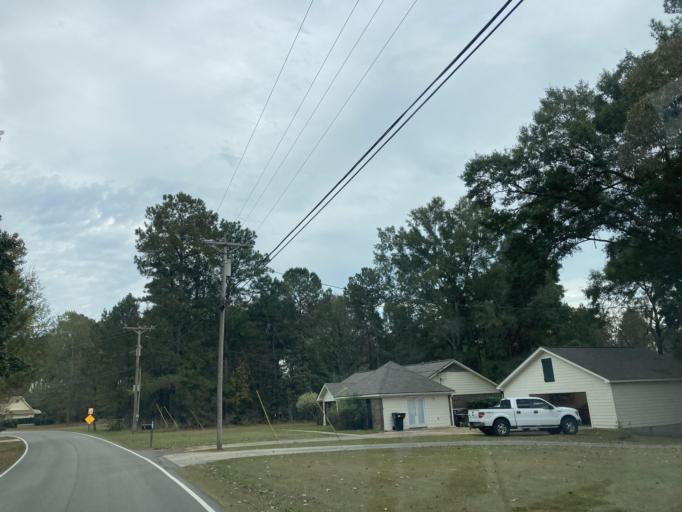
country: US
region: Mississippi
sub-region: Lamar County
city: West Hattiesburg
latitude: 31.2966
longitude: -89.4304
